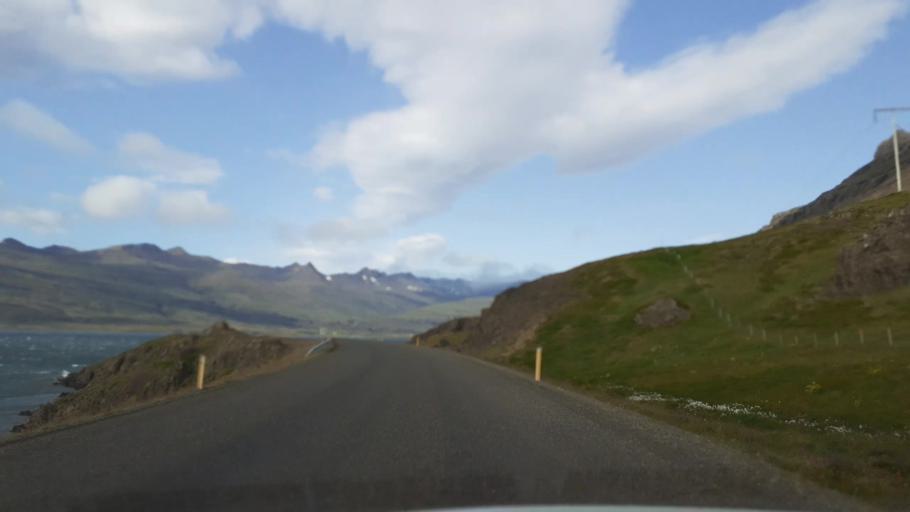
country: IS
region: East
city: Reydarfjoerdur
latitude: 64.6597
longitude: -14.4065
